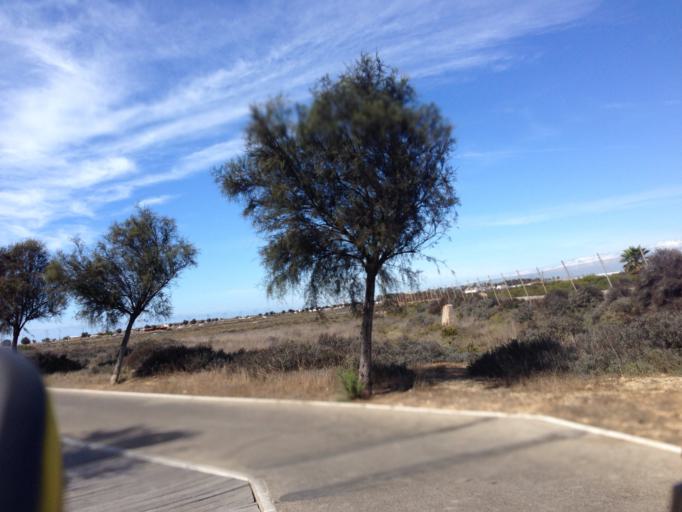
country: ES
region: Andalusia
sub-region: Provincia de Cadiz
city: Chiclana de la Frontera
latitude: 36.3859
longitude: -6.2039
